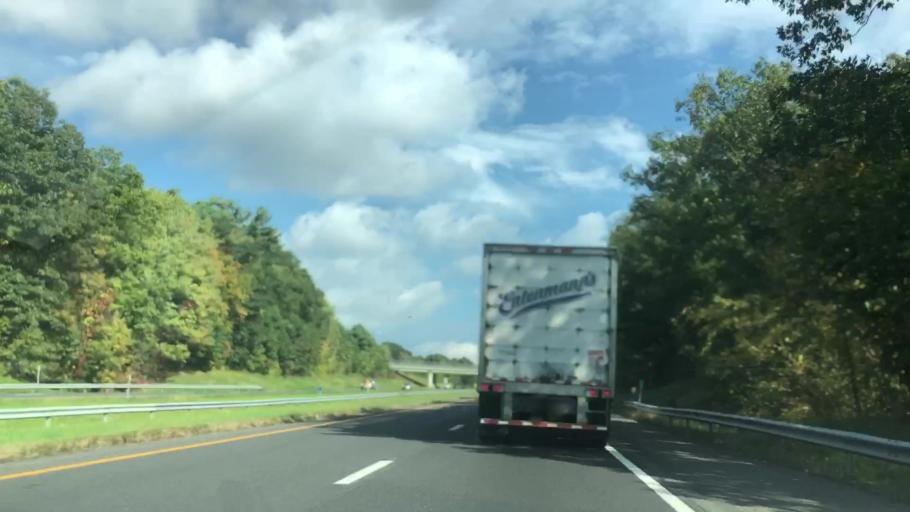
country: US
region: New York
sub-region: Ulster County
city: Lake Katrine
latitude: 41.9975
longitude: -74.0042
